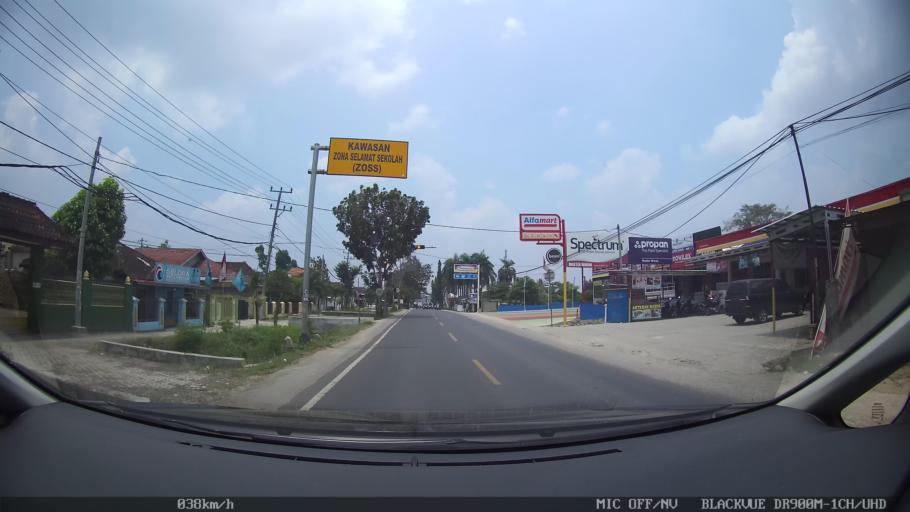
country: ID
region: Lampung
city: Pringsewu
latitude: -5.3551
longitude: 104.9676
